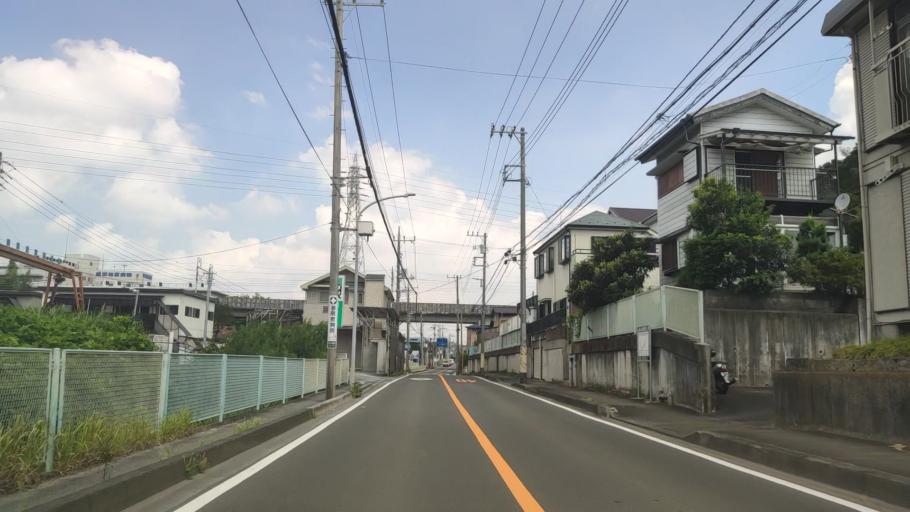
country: JP
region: Kanagawa
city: Minami-rinkan
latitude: 35.4451
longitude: 139.5053
